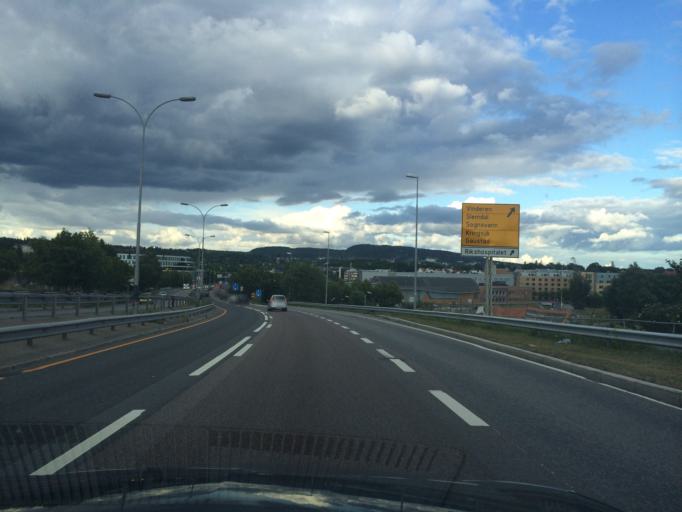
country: NO
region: Oslo
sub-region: Oslo
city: Oslo
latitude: 59.9459
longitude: 10.7181
